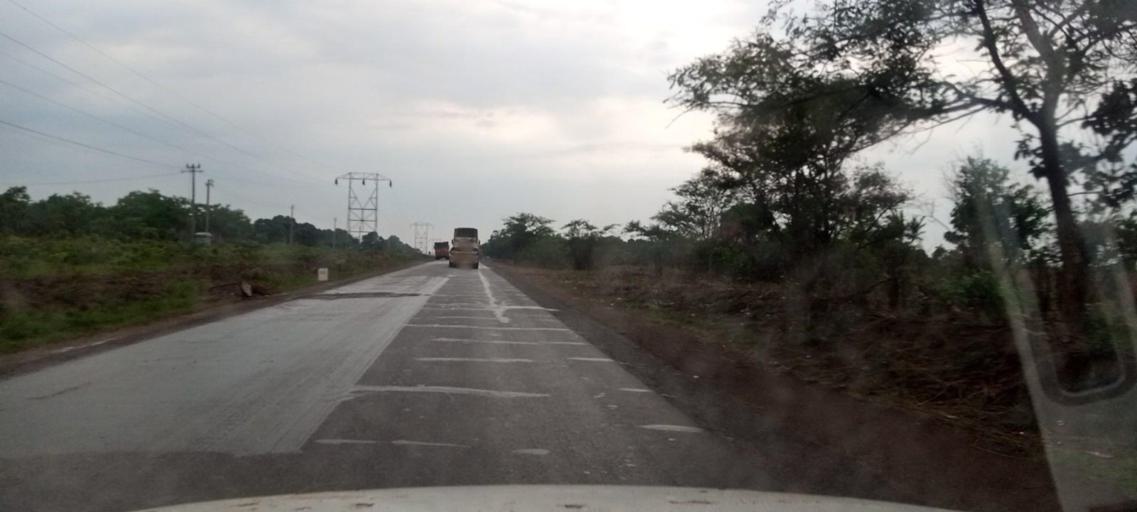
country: CD
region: Katanga
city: Likasi
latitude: -11.0085
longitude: 26.9087
